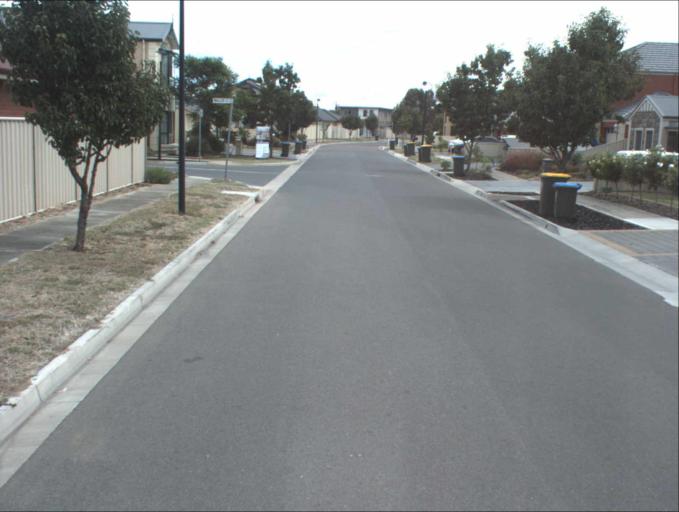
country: AU
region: South Australia
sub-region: Port Adelaide Enfield
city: Birkenhead
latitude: -34.8171
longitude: 138.5030
